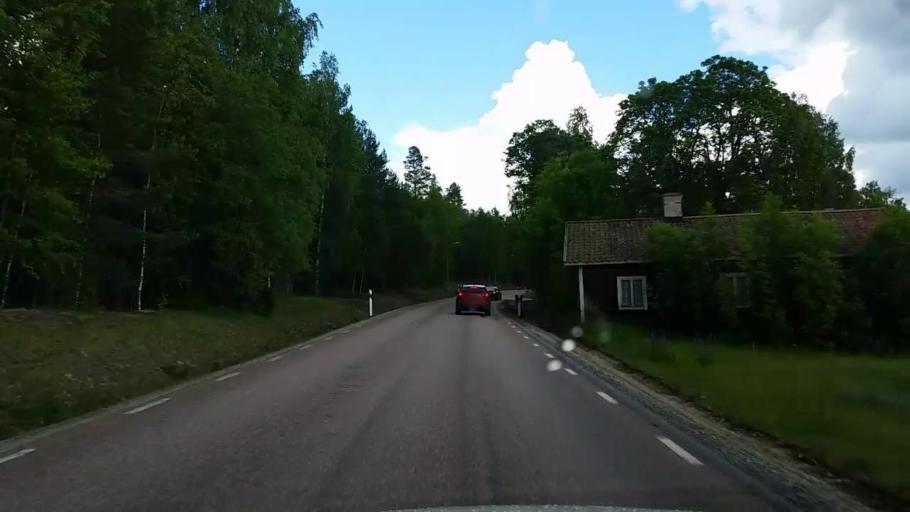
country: SE
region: Vaestmanland
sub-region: Skinnskattebergs Kommun
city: Skinnskatteberg
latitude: 59.8567
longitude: 15.8417
